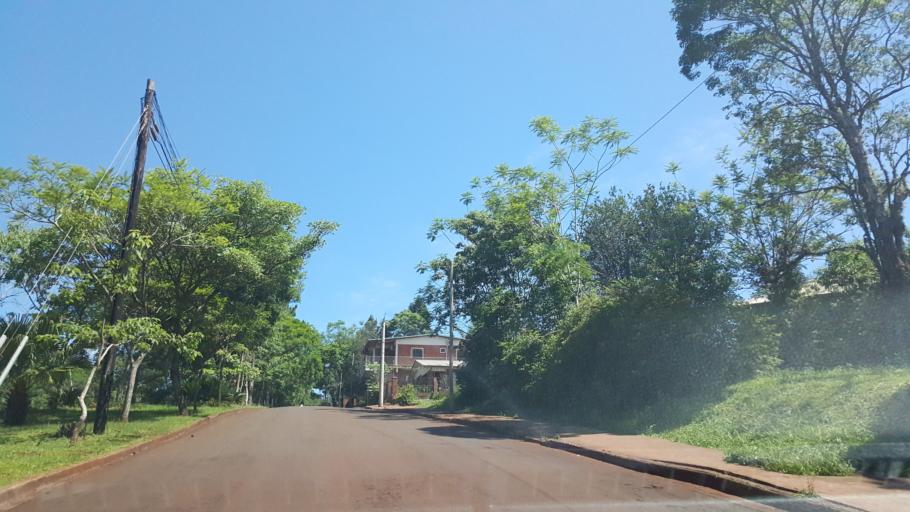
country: AR
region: Misiones
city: Capiovi
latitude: -26.9293
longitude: -55.0605
